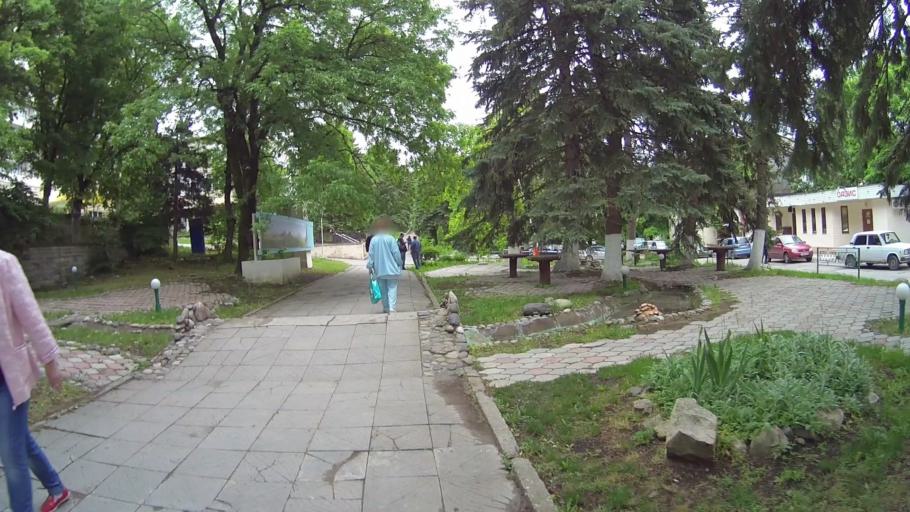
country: RU
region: Stavropol'skiy
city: Zheleznovodsk
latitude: 44.1347
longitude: 43.0272
